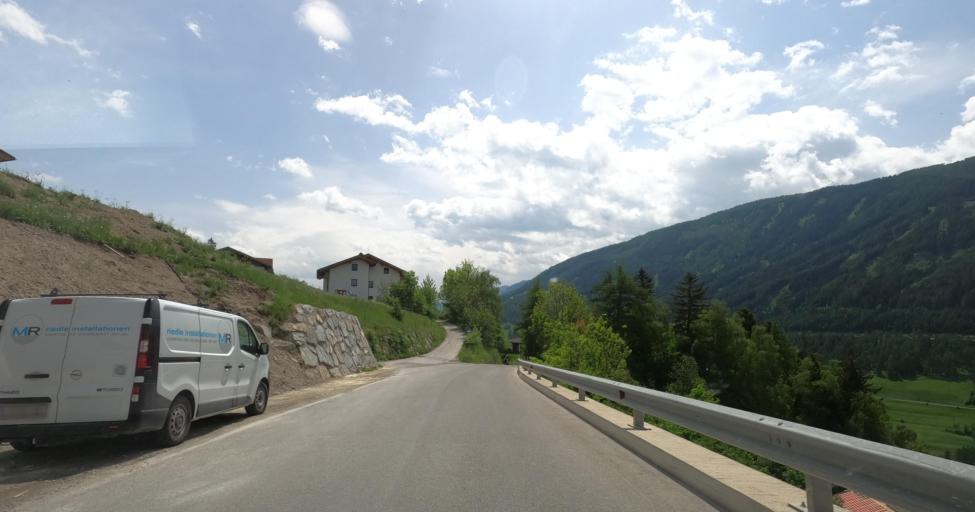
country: AT
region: Tyrol
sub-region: Politischer Bezirk Innsbruck Land
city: Ellbogen
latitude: 47.1740
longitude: 11.4404
